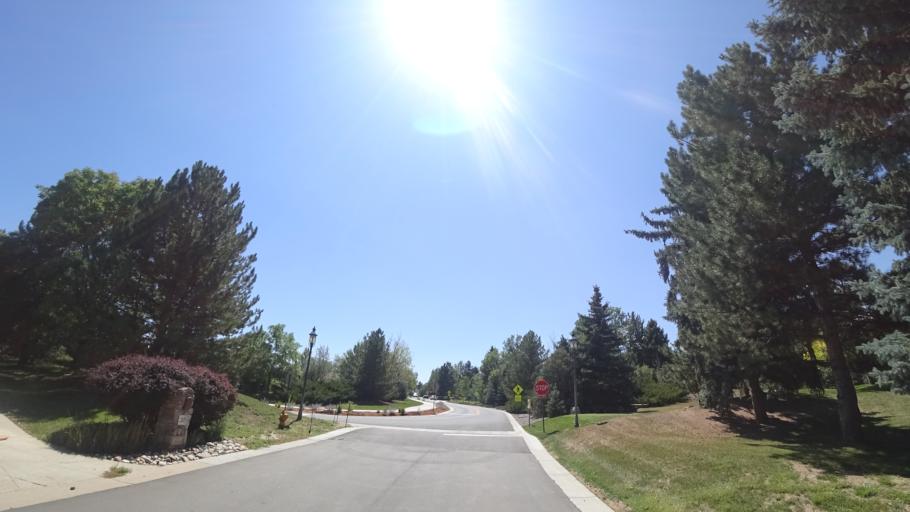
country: US
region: Colorado
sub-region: Arapahoe County
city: Greenwood Village
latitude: 39.6118
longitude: -104.9566
